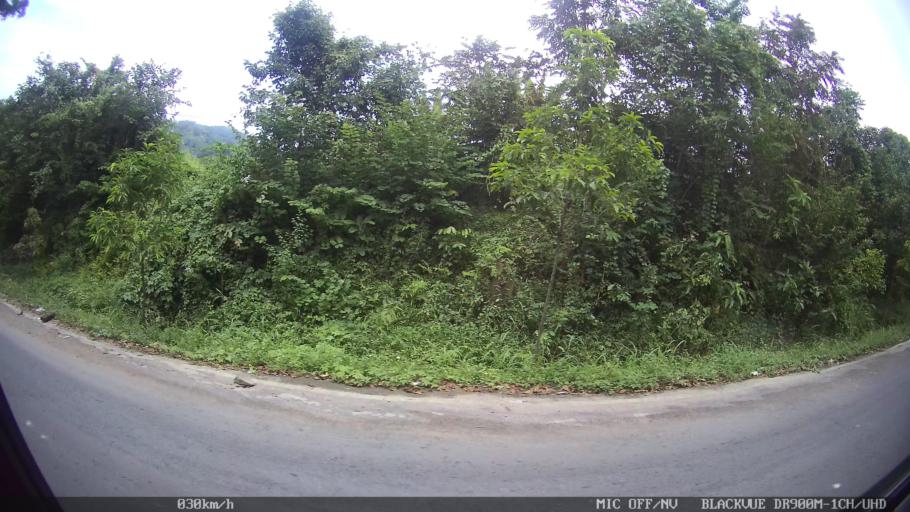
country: ID
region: Lampung
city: Bandarlampung
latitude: -5.4344
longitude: 105.2344
